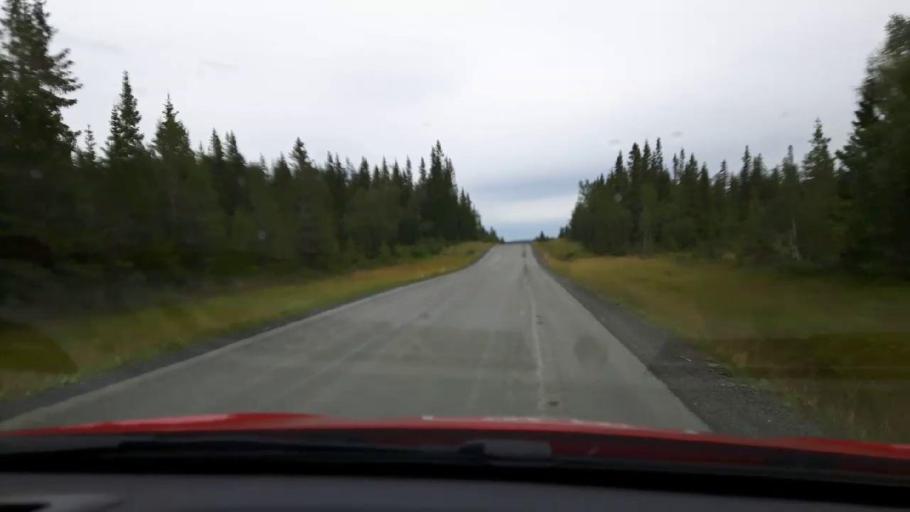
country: SE
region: Jaemtland
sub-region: Are Kommun
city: Are
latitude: 63.4429
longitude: 13.2428
